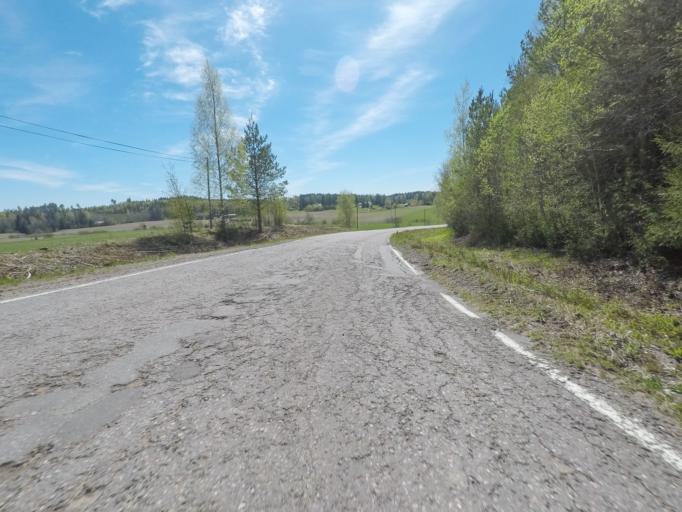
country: FI
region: Uusimaa
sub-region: Helsinki
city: Kaerkoelae
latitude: 60.5860
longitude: 23.7971
